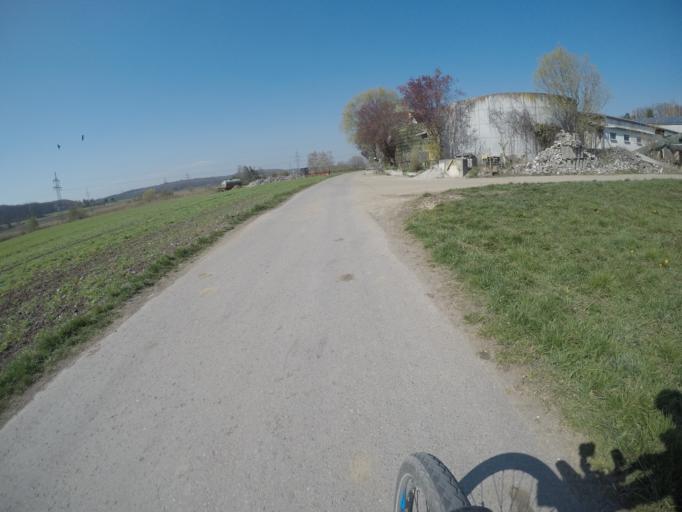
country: DE
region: Baden-Wuerttemberg
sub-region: Regierungsbezirk Stuttgart
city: Renningen
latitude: 48.7640
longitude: 8.9644
